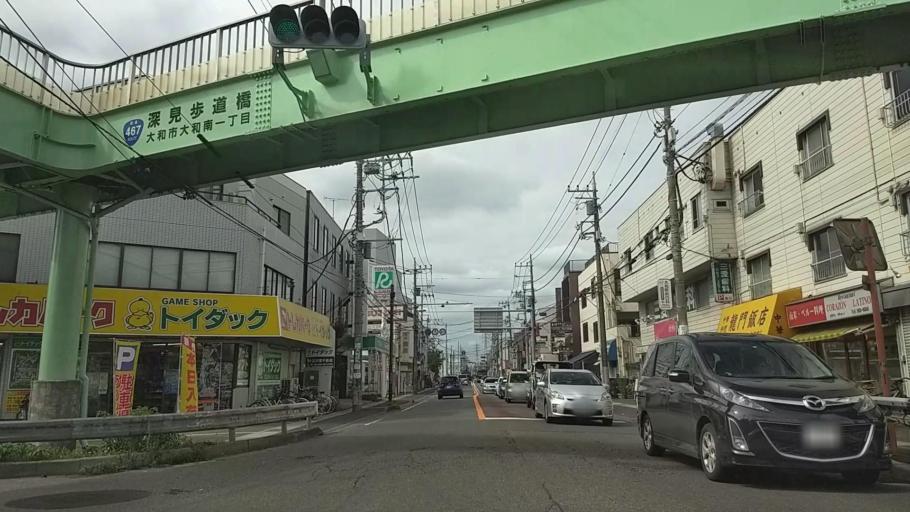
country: JP
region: Kanagawa
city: Minami-rinkan
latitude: 35.4680
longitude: 139.4661
